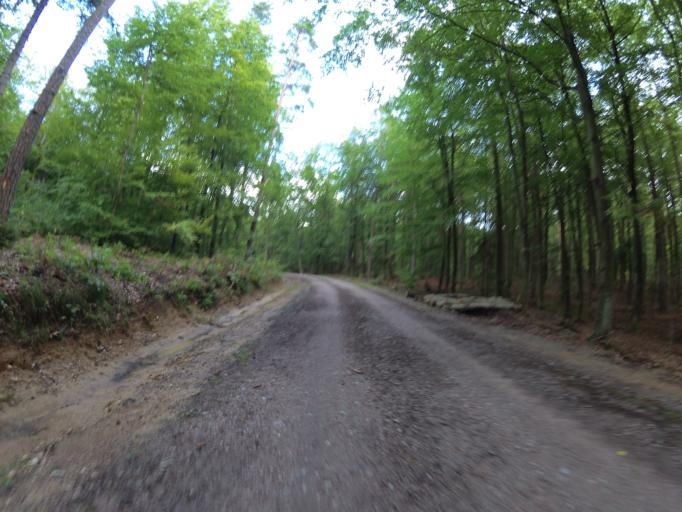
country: PL
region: Pomeranian Voivodeship
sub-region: Powiat wejherowski
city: Bojano
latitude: 54.5082
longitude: 18.4191
